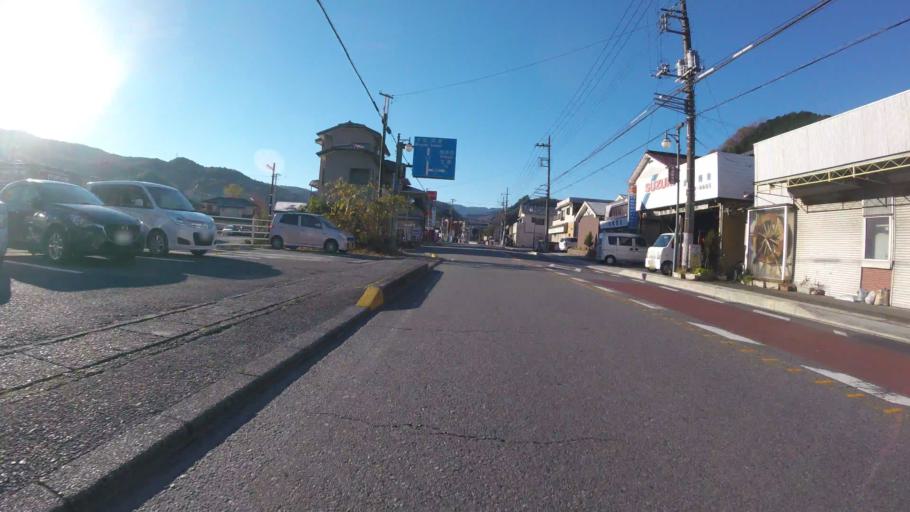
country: JP
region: Shizuoka
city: Heda
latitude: 34.9295
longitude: 138.9331
